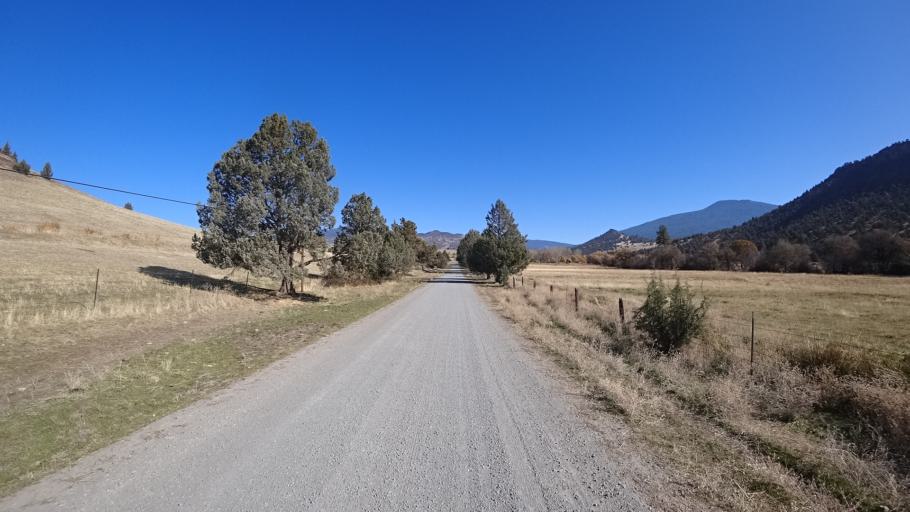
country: US
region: California
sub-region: Siskiyou County
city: Montague
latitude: 41.7374
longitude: -122.3454
